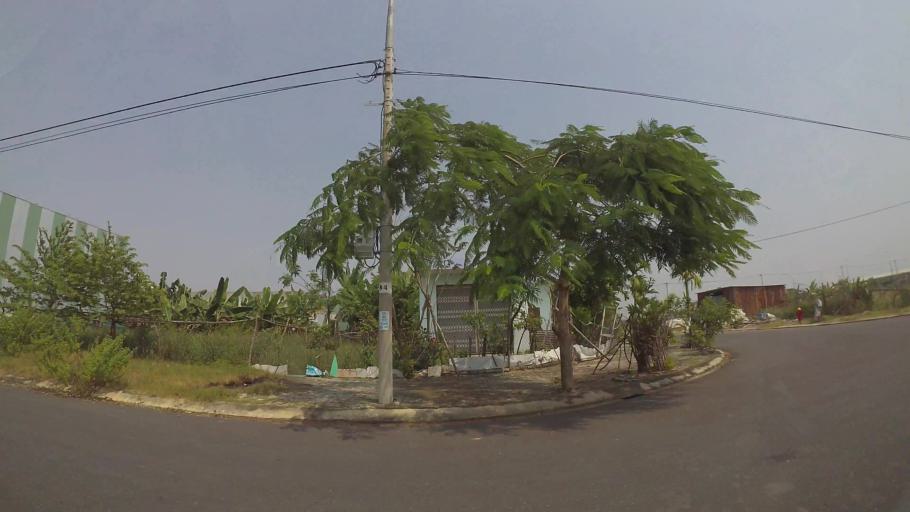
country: VN
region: Da Nang
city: Cam Le
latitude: 15.9785
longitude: 108.2116
